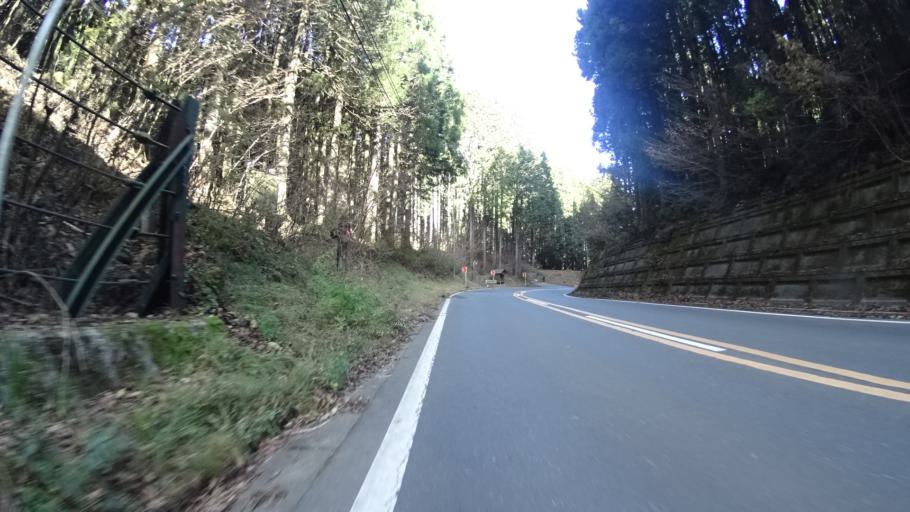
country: JP
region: Saitama
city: Chichibu
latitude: 35.9314
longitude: 139.1522
